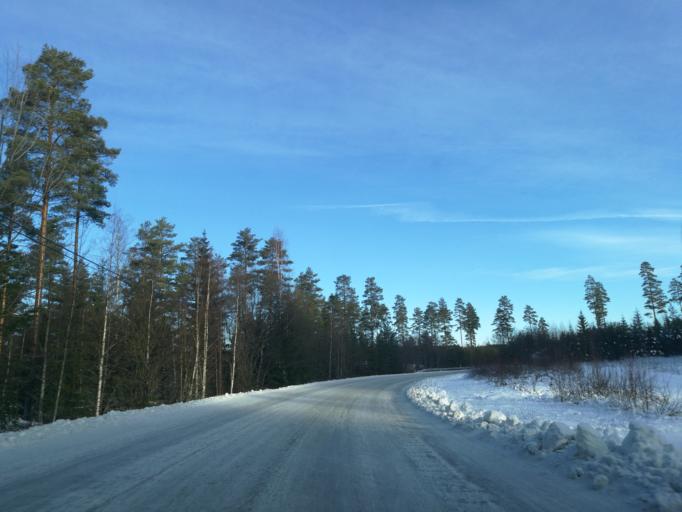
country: NO
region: Hedmark
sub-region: Grue
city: Kirkenaer
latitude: 60.3415
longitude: 12.2964
